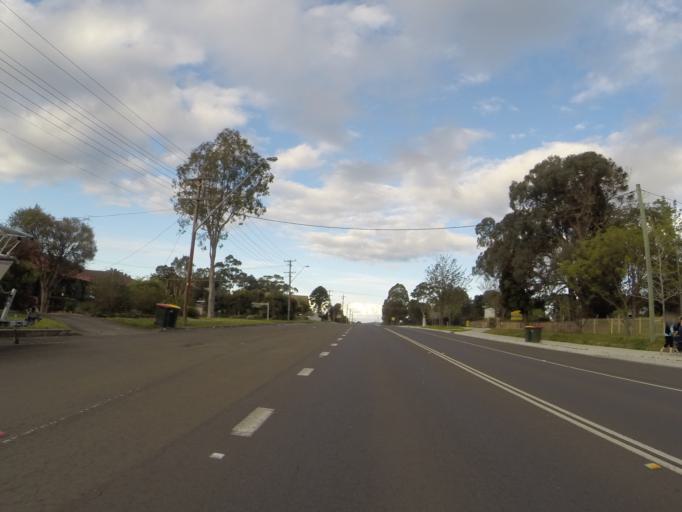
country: AU
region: New South Wales
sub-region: Shellharbour
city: Albion Park Rail
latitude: -34.5719
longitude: 150.7606
